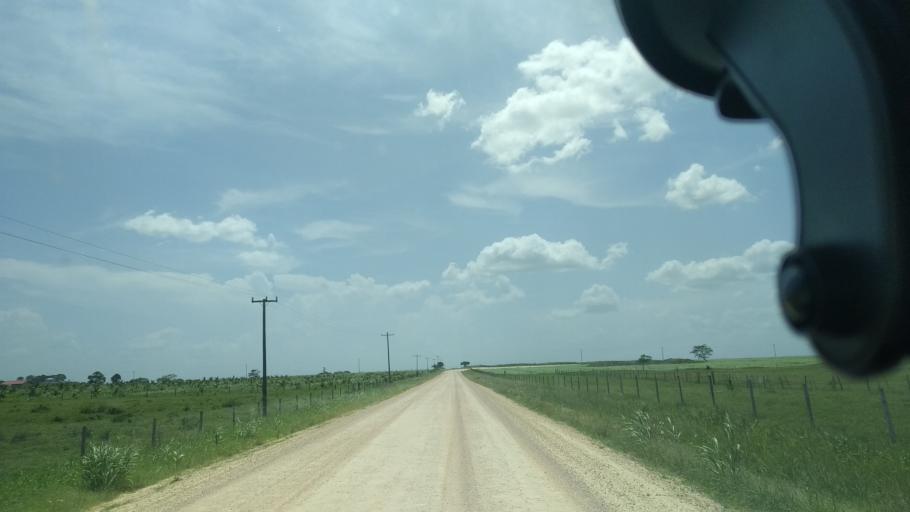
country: BZ
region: Cayo
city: San Ignacio
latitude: 17.3148
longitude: -89.0433
